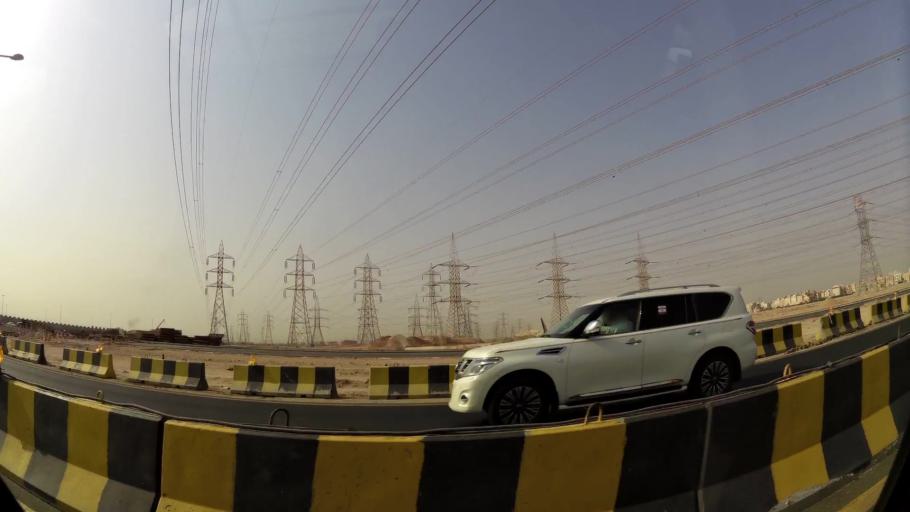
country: KW
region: Muhafazat al Jahra'
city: Al Jahra'
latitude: 29.3381
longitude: 47.7957
